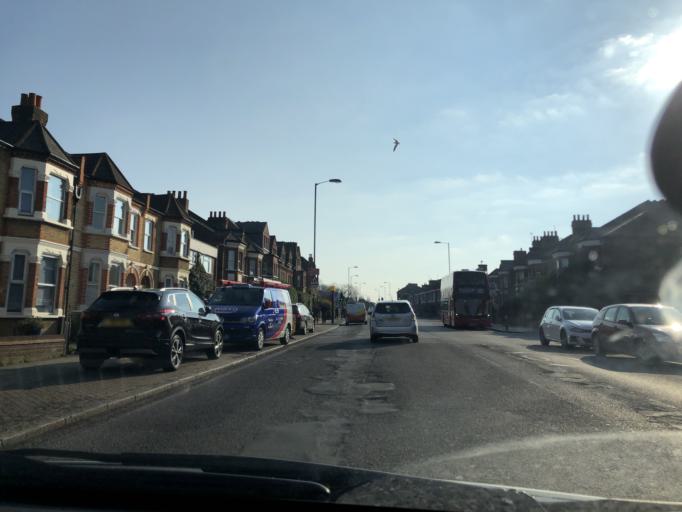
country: GB
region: England
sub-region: Greater London
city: Catford
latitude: 51.4496
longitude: -0.0407
